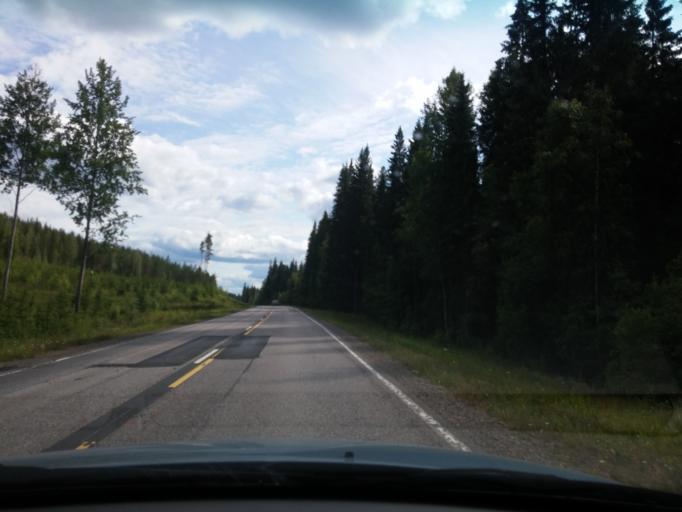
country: FI
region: Central Finland
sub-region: Keuruu
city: Multia
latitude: 62.3494
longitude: 24.7376
